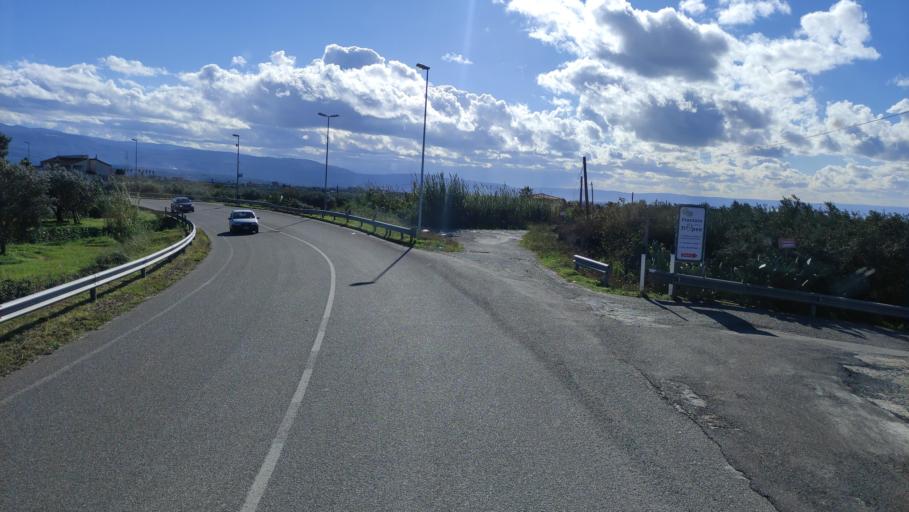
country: IT
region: Calabria
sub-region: Provincia di Catanzaro
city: Nicastro-Sambiase
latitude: 38.9394
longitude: 16.2819
